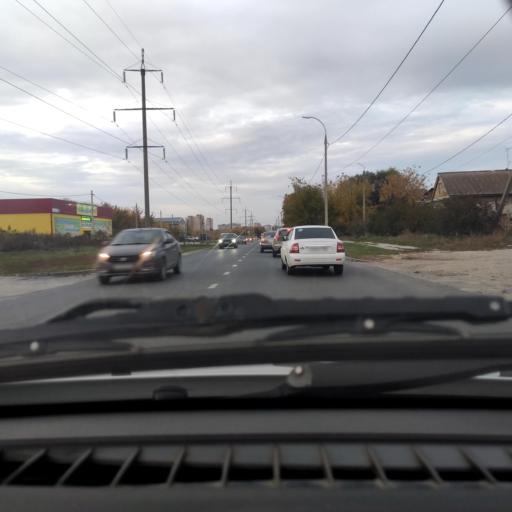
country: RU
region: Samara
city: Tol'yatti
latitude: 53.5201
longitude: 49.3958
